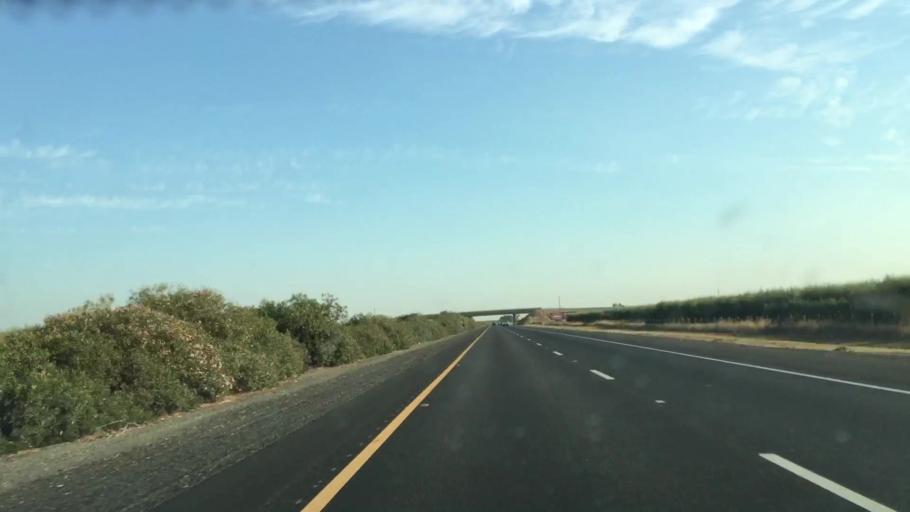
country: US
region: California
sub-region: Glenn County
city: Willows
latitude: 39.6072
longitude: -122.2077
